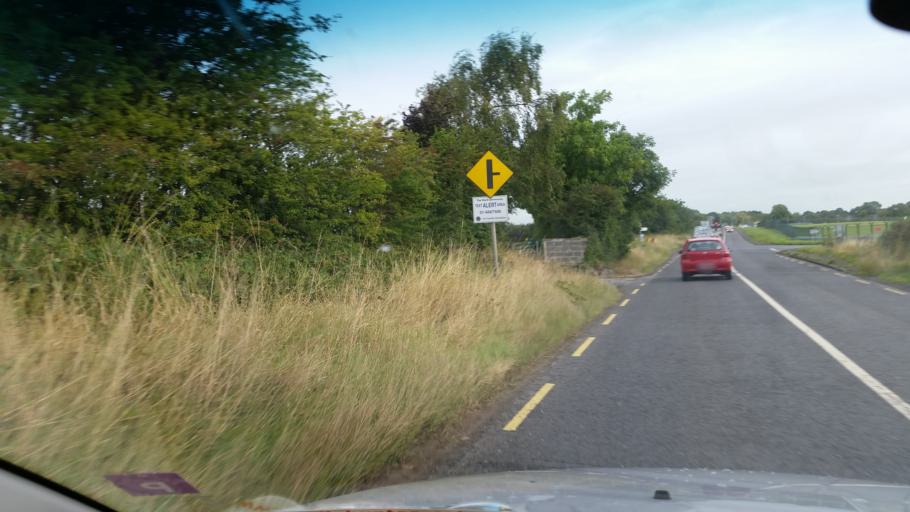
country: IE
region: Leinster
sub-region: Dublin City
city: Finglas
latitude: 53.4212
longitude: -6.3068
